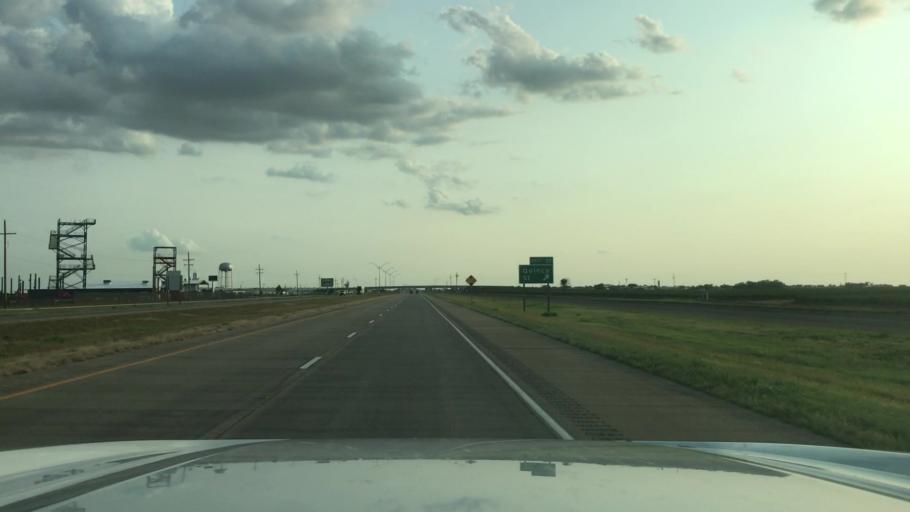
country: US
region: Texas
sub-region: Hale County
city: Seth Ward
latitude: 34.2248
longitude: -101.7192
